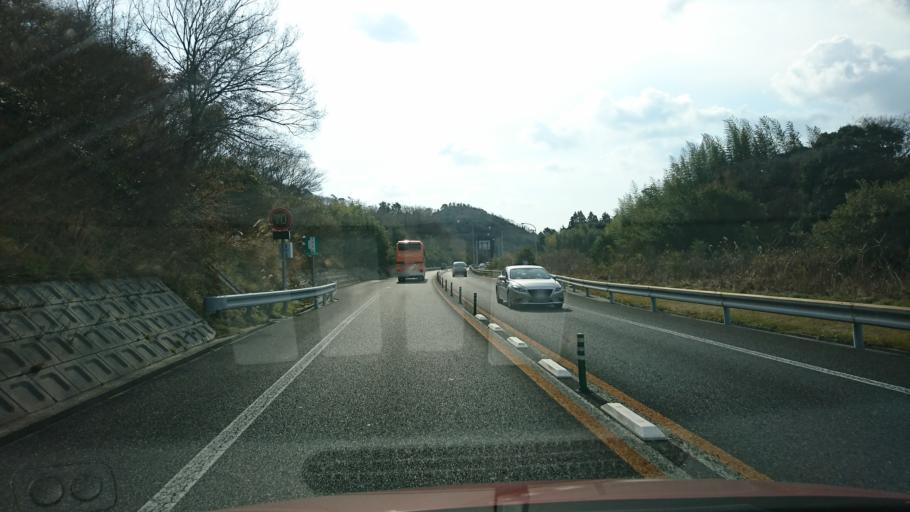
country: JP
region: Hiroshima
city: Innoshima
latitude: 34.2033
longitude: 133.0790
